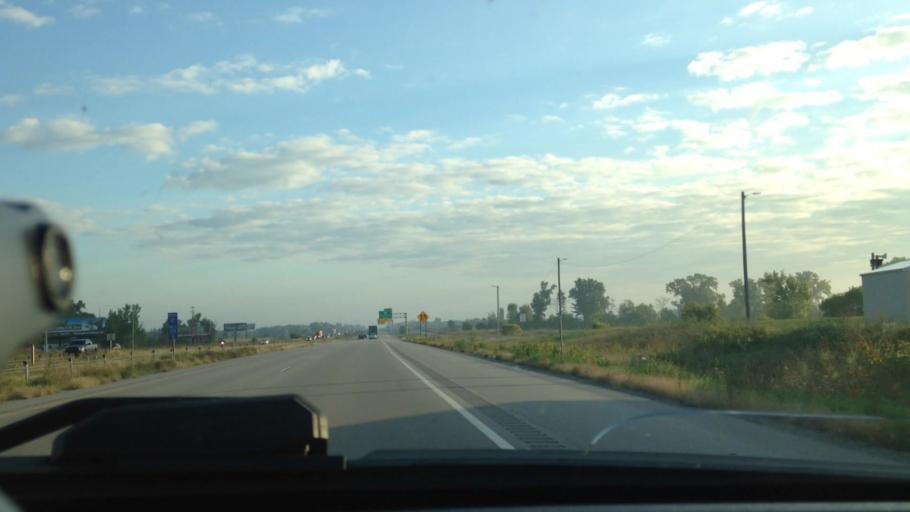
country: US
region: Wisconsin
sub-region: Brown County
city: Wrightstown
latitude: 44.3413
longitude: -88.2003
